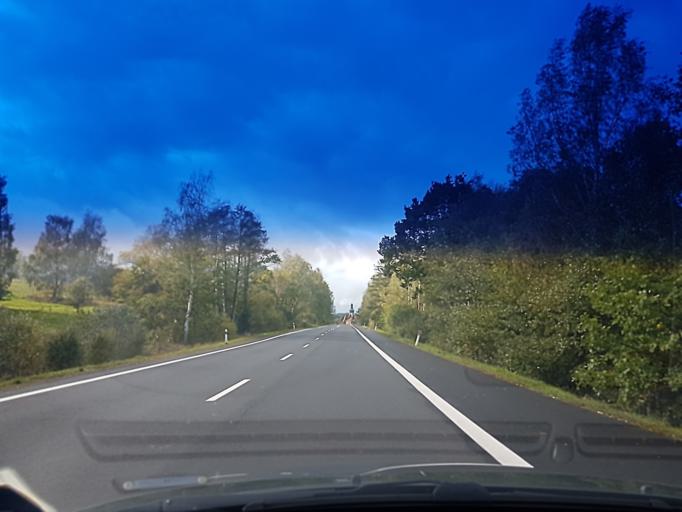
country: DE
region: Bavaria
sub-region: Upper Franconia
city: Schirnding
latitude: 50.0853
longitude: 12.2936
